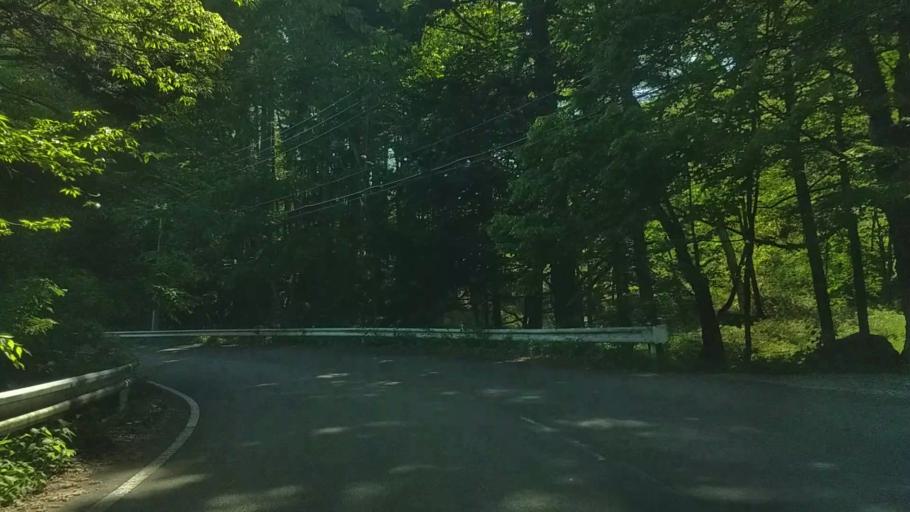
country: JP
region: Yamanashi
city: Nirasaki
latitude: 35.8822
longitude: 138.3673
